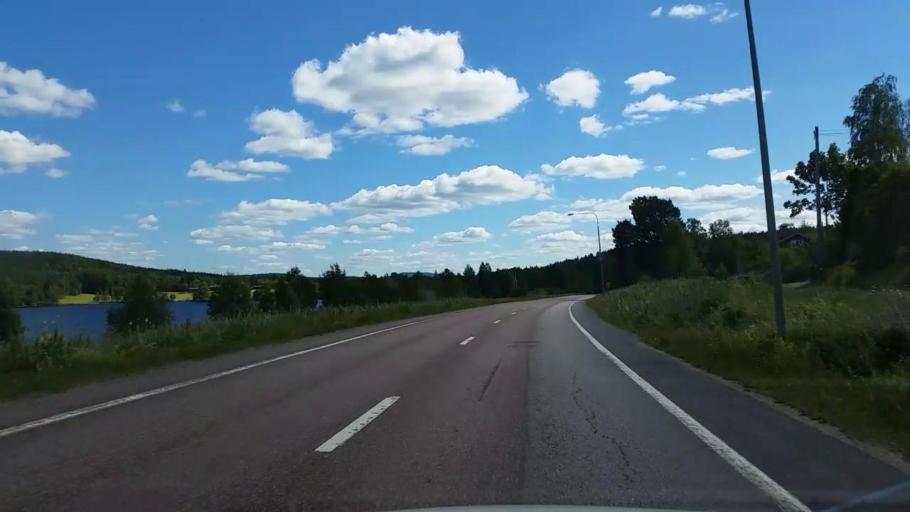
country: SE
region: Dalarna
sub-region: Faluns Kommun
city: Svardsjo
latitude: 60.8549
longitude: 15.7515
